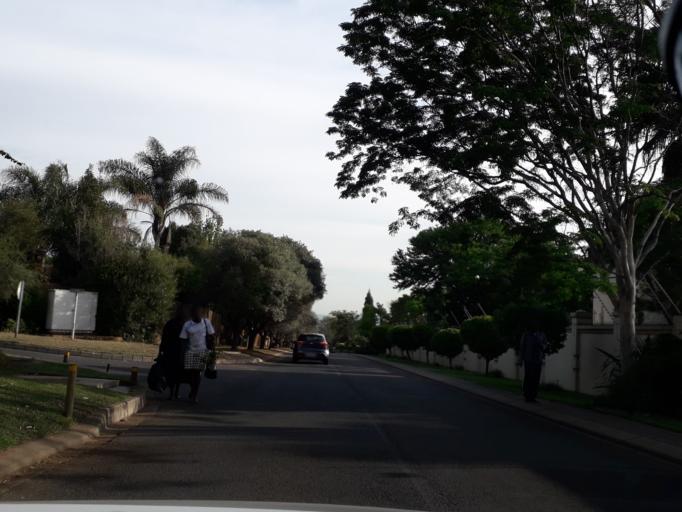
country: ZA
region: Gauteng
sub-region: City of Johannesburg Metropolitan Municipality
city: Diepsloot
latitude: -26.0313
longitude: 27.9911
